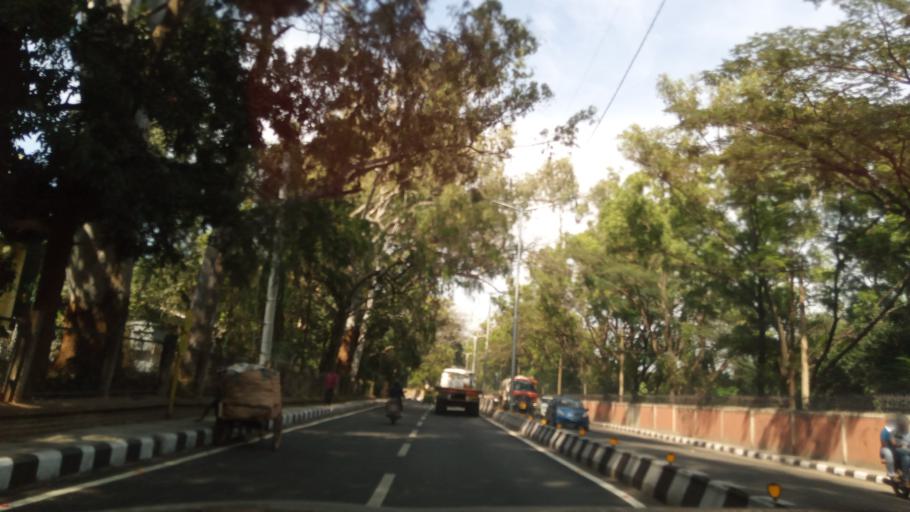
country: IN
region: Karnataka
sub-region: Bangalore Urban
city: Bangalore
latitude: 13.0344
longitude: 77.5411
